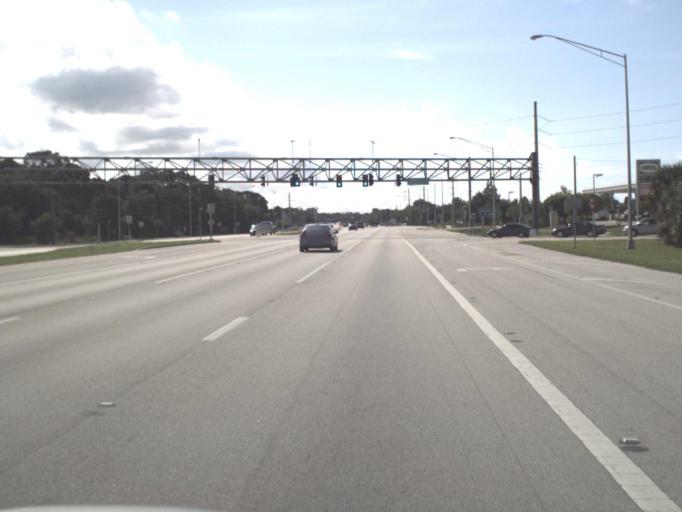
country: US
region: Florida
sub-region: Sarasota County
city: Laurel
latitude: 27.1428
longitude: -82.4610
